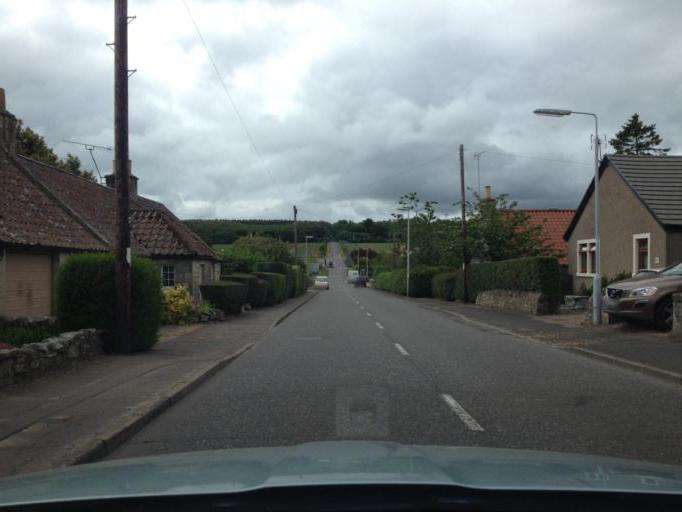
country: GB
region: Scotland
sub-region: Fife
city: Strathkinness
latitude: 56.3318
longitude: -2.8763
